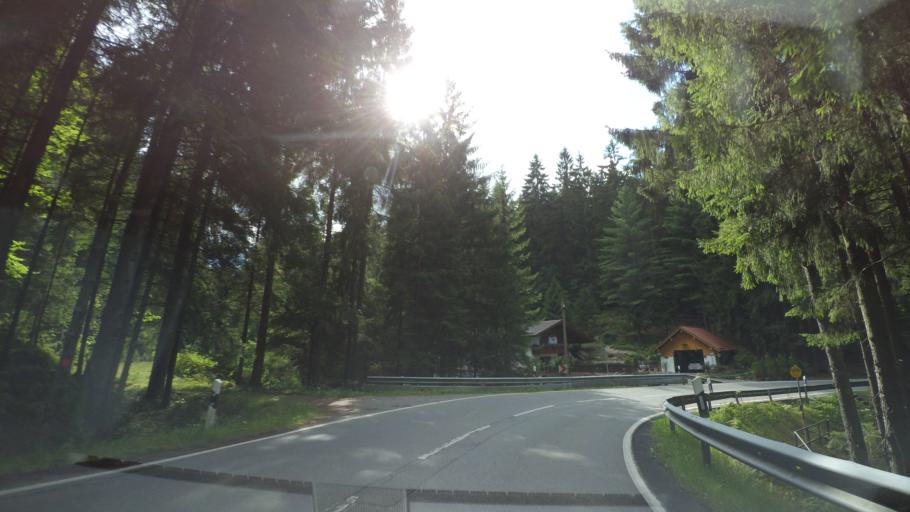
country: DE
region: Bavaria
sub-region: Upper Palatinate
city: Arrach
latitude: 49.1822
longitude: 13.0056
